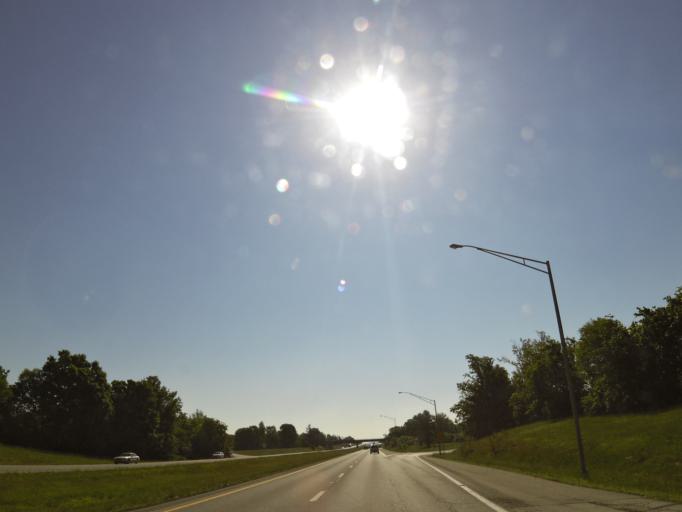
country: US
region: Kentucky
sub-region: Shelby County
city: Shelbyville
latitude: 38.1847
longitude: -85.2174
